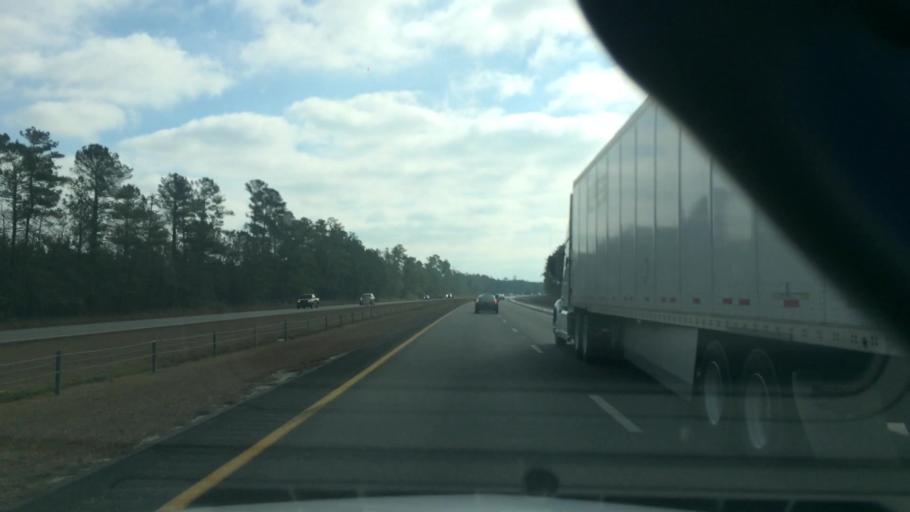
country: US
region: North Carolina
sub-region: Pender County
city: Burgaw
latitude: 34.5572
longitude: -77.8949
